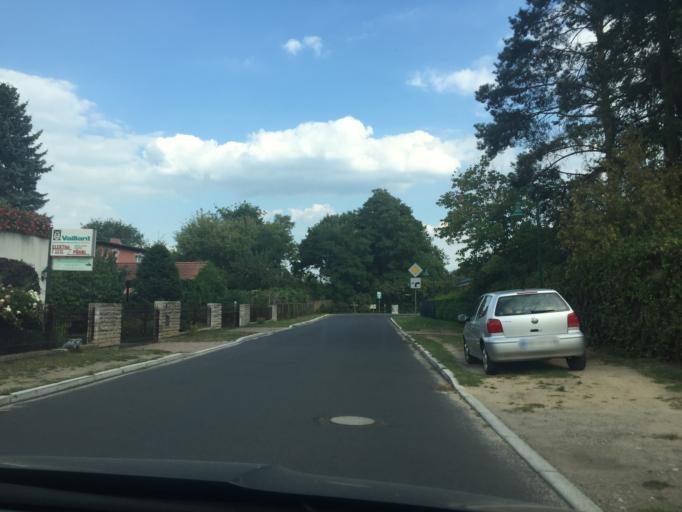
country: DE
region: Brandenburg
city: Erkner
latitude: 52.3833
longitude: 13.7688
